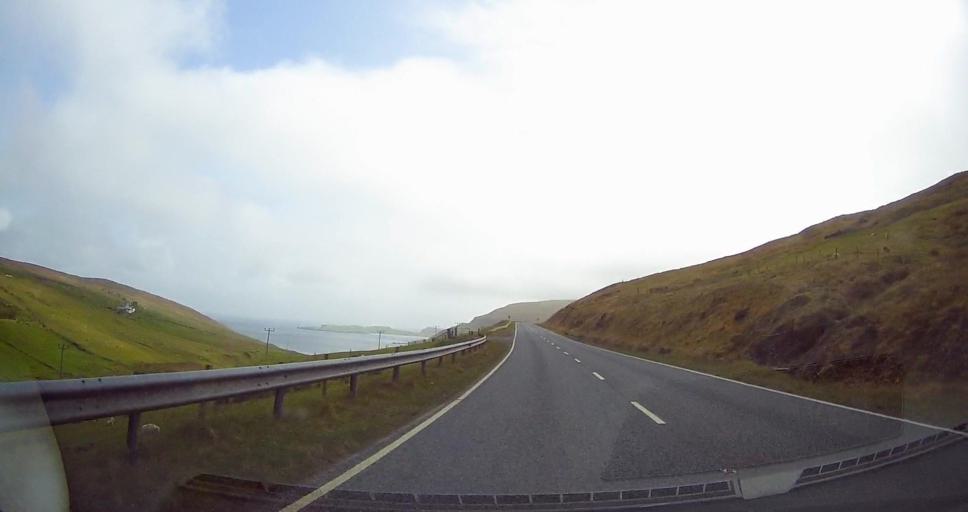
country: GB
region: Scotland
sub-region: Shetland Islands
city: Sandwick
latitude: 59.9981
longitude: -1.2797
